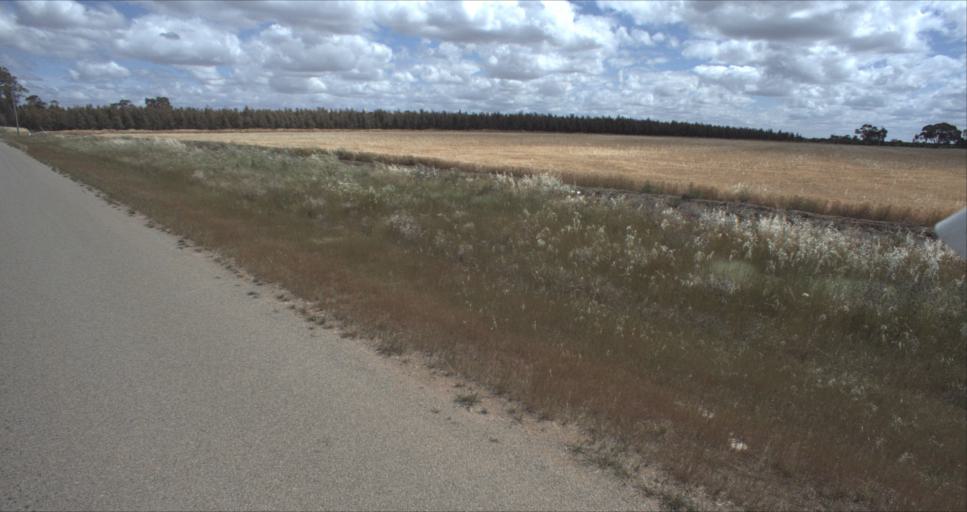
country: AU
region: New South Wales
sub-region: Leeton
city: Leeton
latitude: -34.5726
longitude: 146.3988
